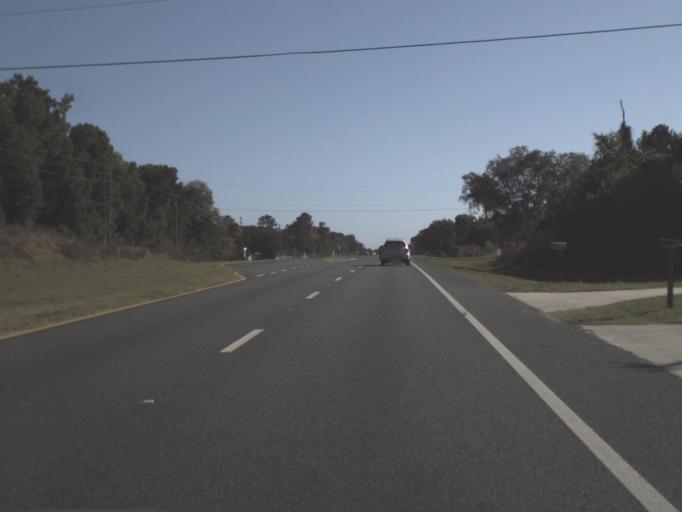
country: US
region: Florida
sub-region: Marion County
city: Belleview
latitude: 29.0259
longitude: -82.0854
